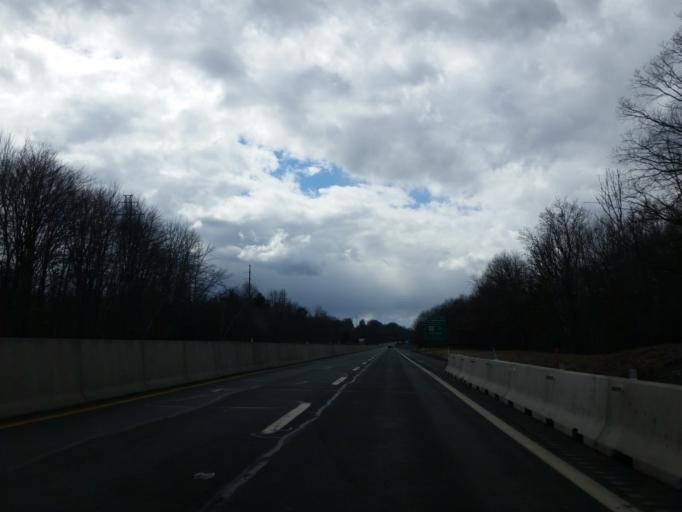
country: US
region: Pennsylvania
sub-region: Luzerne County
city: Dupont
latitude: 41.3234
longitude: -75.7319
